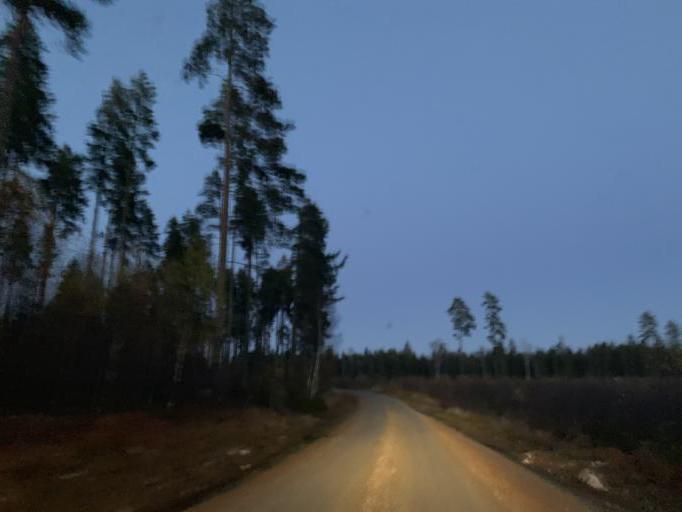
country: SE
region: OErebro
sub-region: Lindesbergs Kommun
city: Fellingsbro
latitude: 59.3811
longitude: 15.6679
